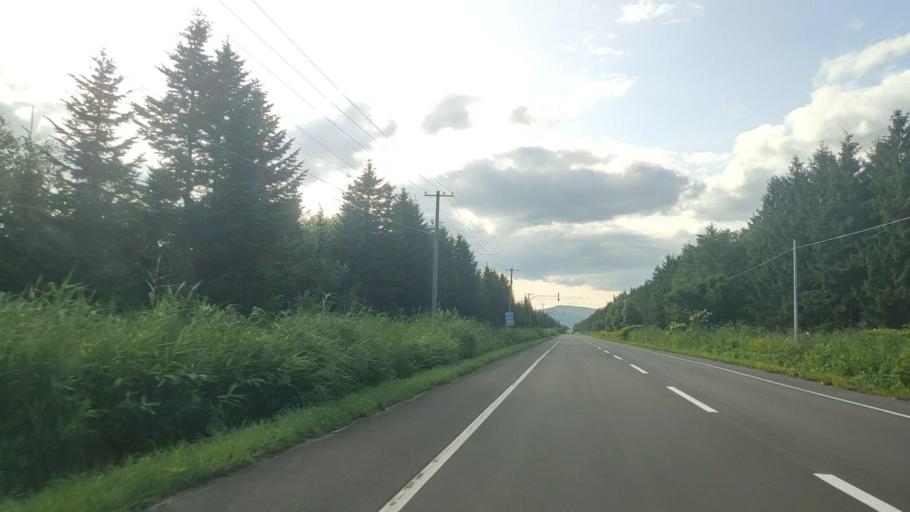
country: JP
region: Hokkaido
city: Makubetsu
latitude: 44.8854
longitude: 142.0112
